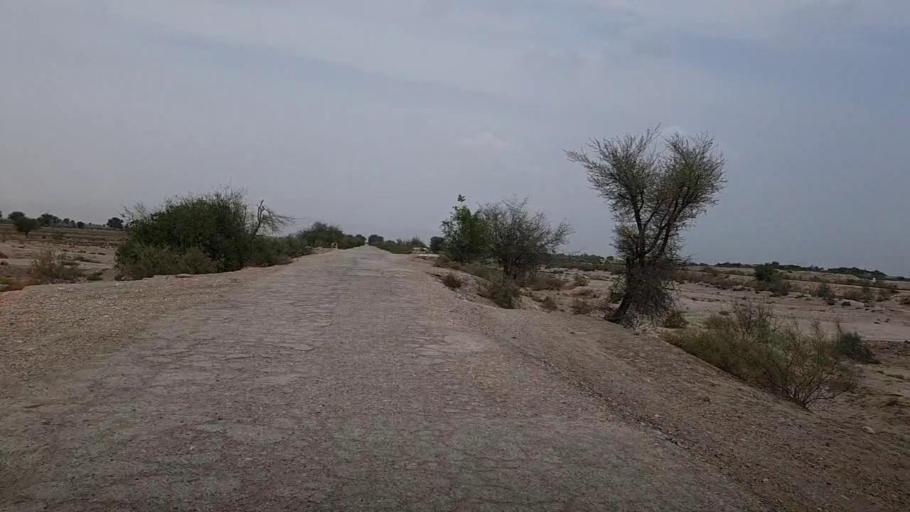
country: PK
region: Sindh
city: Sann
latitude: 26.2008
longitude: 67.9730
